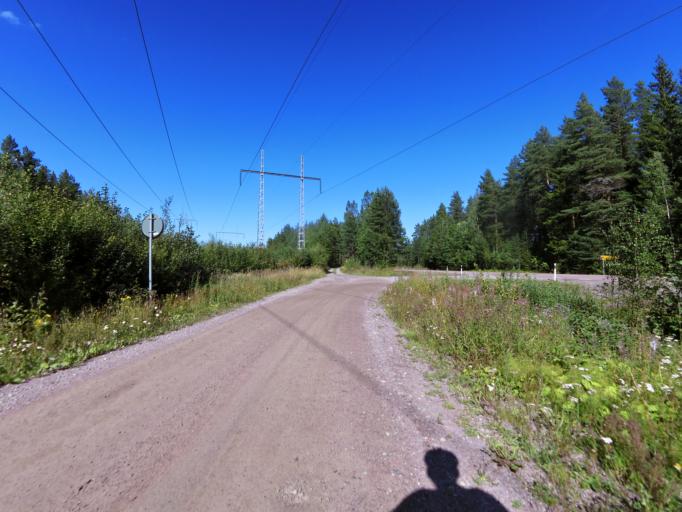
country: SE
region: Gaevleborg
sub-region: Hofors Kommun
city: Hofors
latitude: 60.5460
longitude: 16.4698
